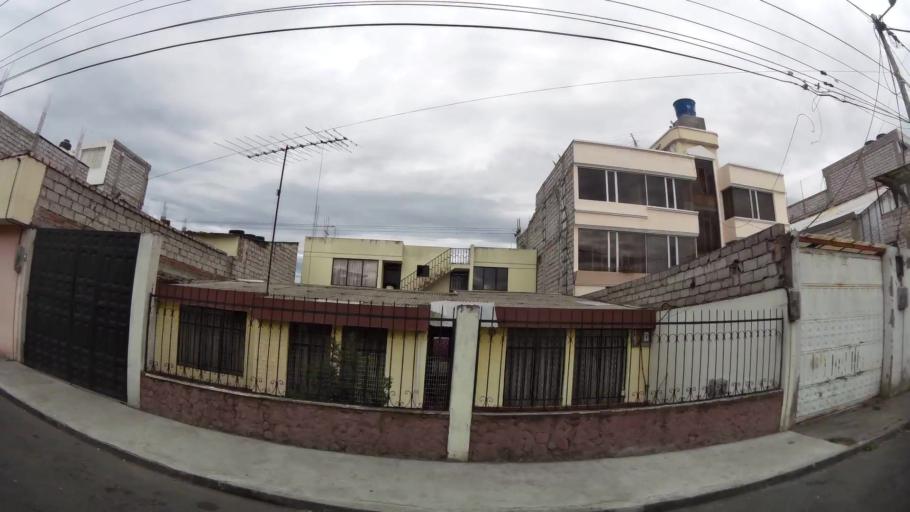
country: EC
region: Cotopaxi
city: Latacunga
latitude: -0.9296
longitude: -78.6248
